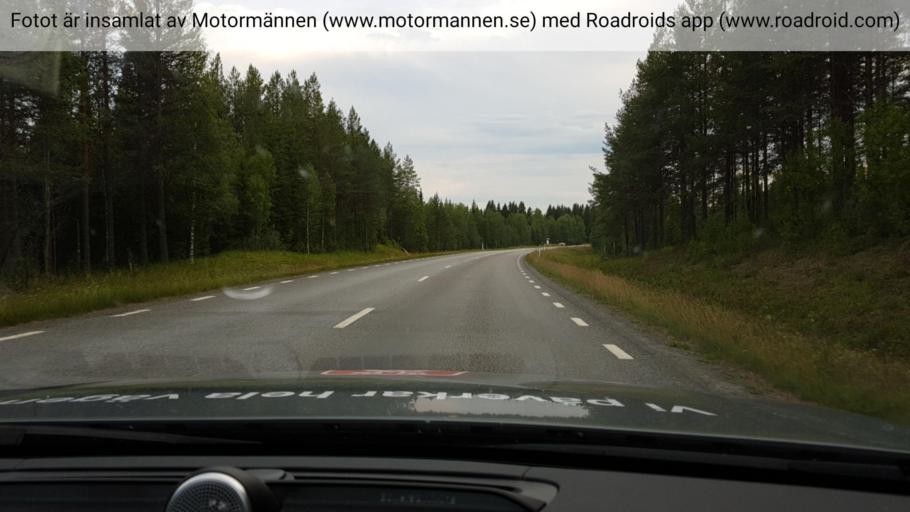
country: SE
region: Jaemtland
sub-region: OEstersunds Kommun
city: Lit
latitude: 63.4861
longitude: 15.2380
